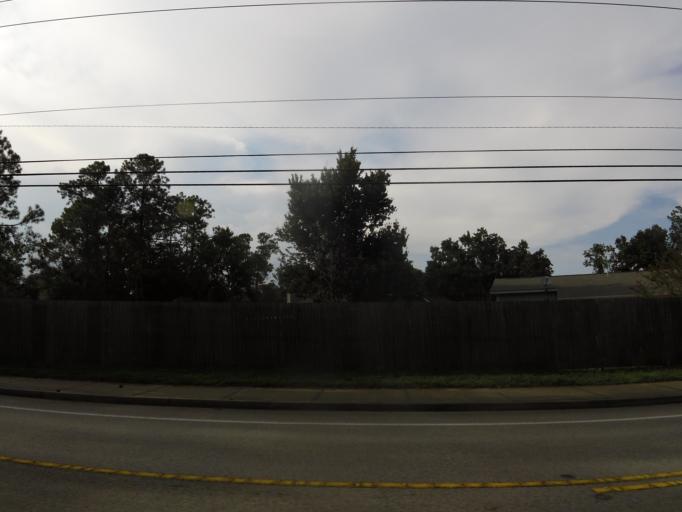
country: US
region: Florida
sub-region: Saint Johns County
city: Fruit Cove
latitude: 30.1842
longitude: -81.6035
